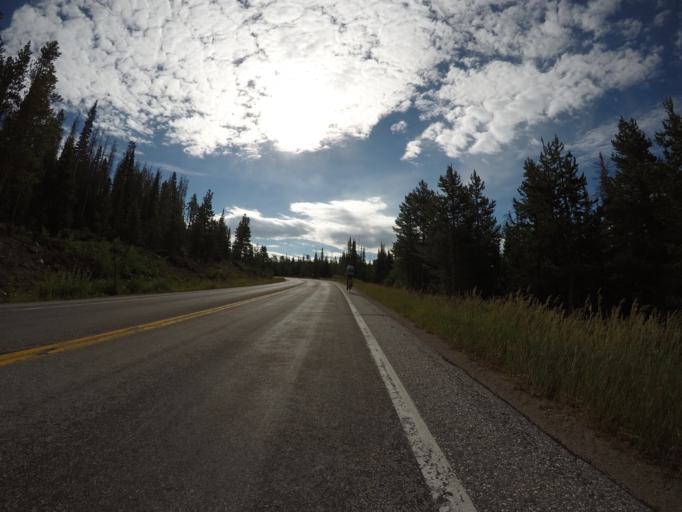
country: US
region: Wyoming
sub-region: Carbon County
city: Saratoga
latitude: 41.3270
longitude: -106.4924
